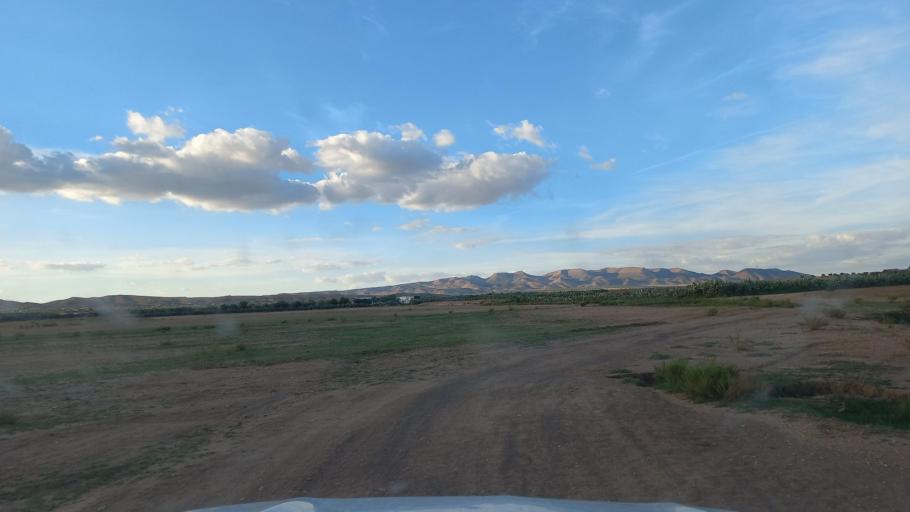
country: TN
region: Al Qasrayn
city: Sbiba
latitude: 35.3529
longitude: 9.0317
